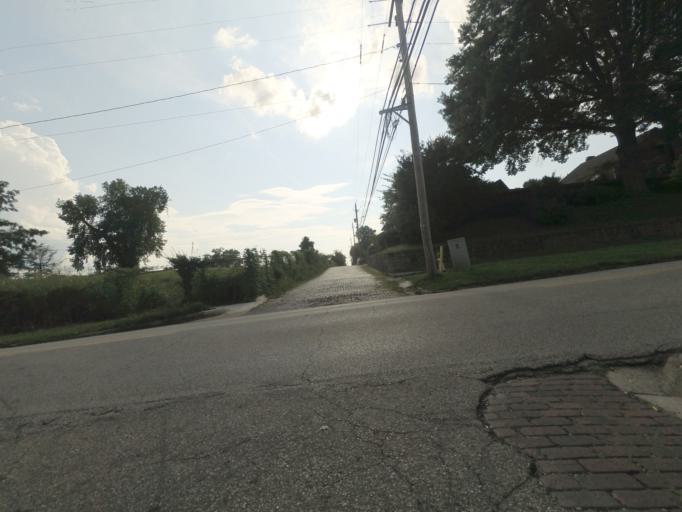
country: US
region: West Virginia
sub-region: Cabell County
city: Huntington
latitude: 38.4285
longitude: -82.4025
